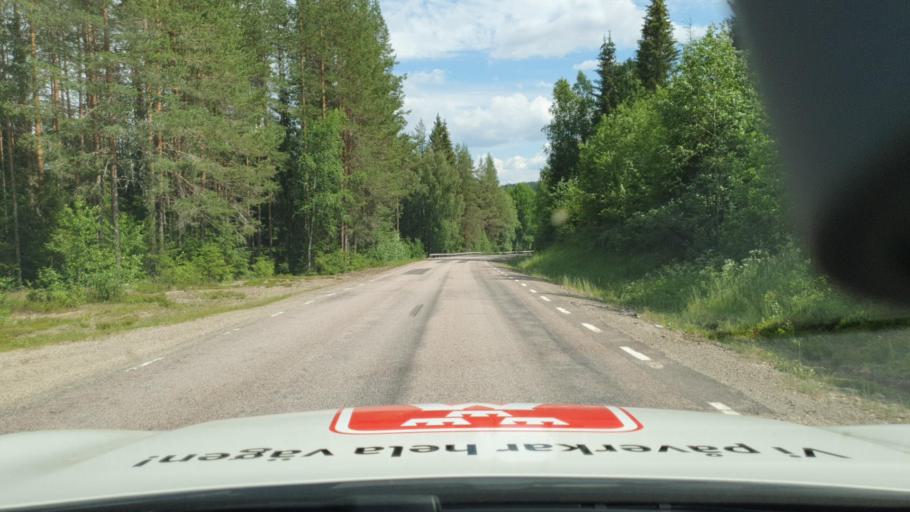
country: SE
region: Vaermland
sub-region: Torsby Kommun
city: Torsby
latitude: 60.7506
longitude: 12.7671
